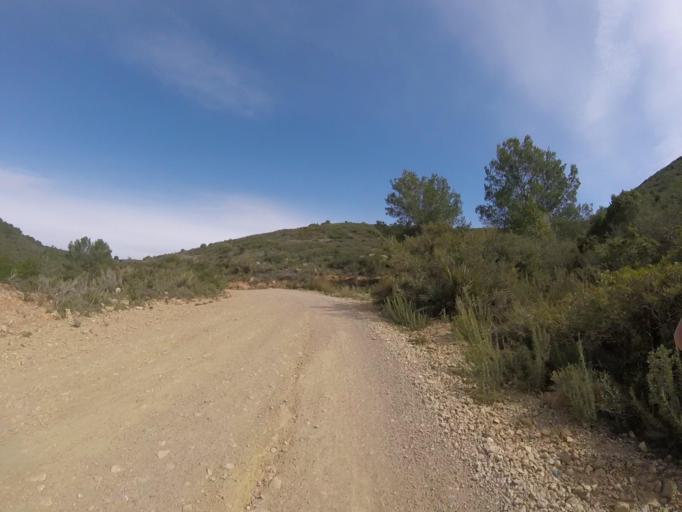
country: ES
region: Valencia
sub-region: Provincia de Castello
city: Torreblanca
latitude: 40.2021
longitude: 0.1518
